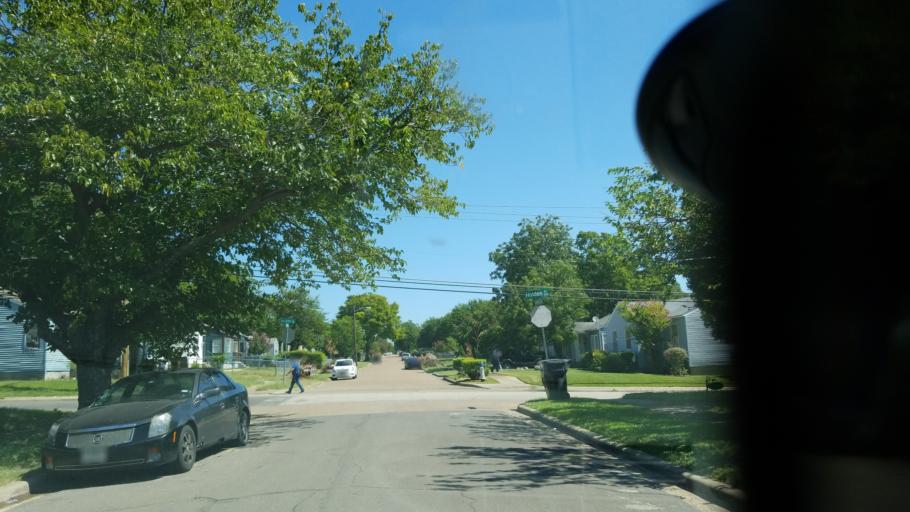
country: US
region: Texas
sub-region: Dallas County
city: Cockrell Hill
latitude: 32.7027
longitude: -96.8206
